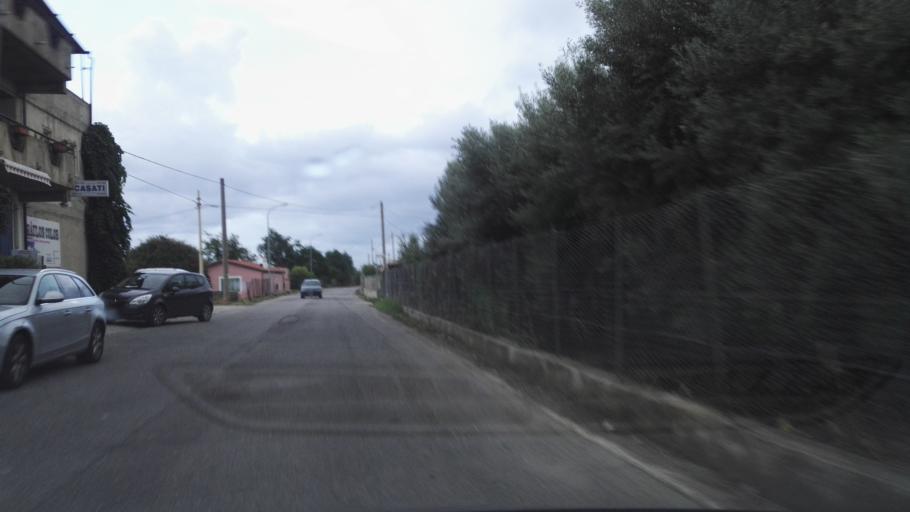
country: IT
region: Calabria
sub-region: Provincia di Reggio Calabria
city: Caulonia Marina
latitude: 38.3571
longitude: 16.4698
